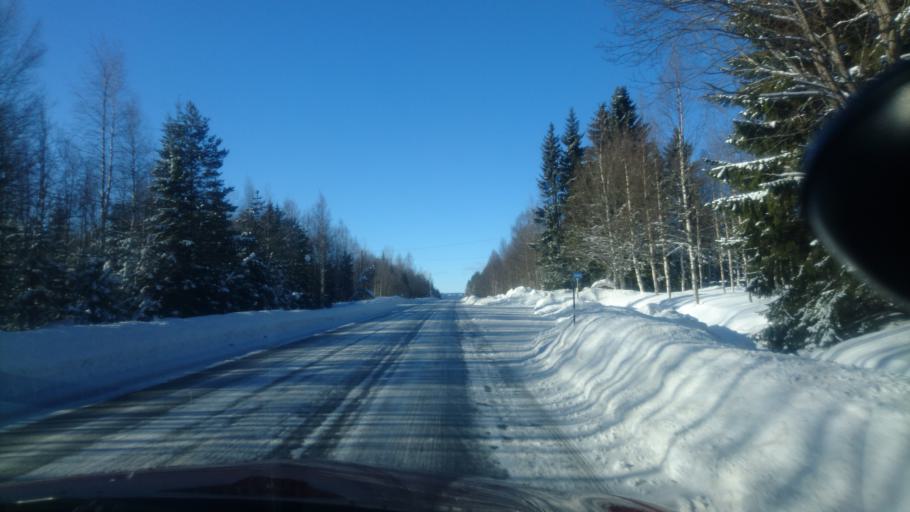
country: NO
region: Hedmark
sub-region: Trysil
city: Innbygda
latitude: 61.2650
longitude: 12.4320
